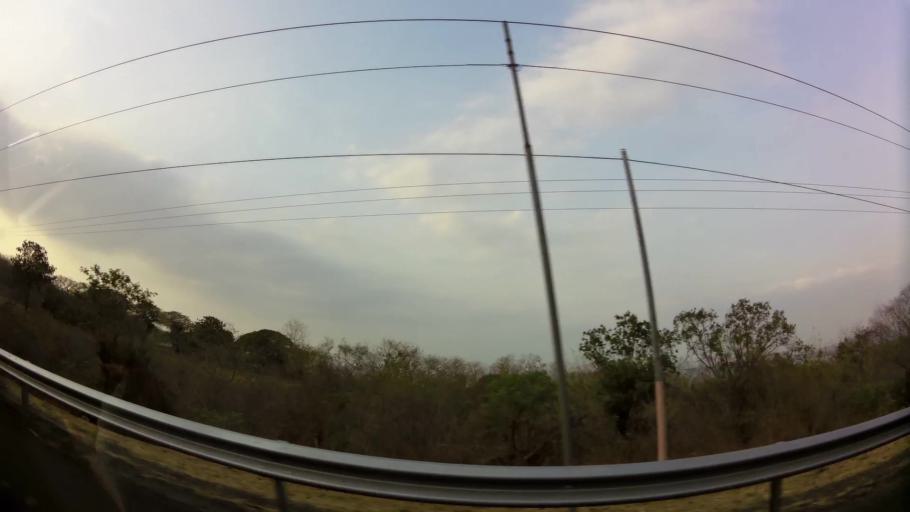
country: NI
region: Leon
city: Nagarote
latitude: 12.2443
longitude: -86.4429
